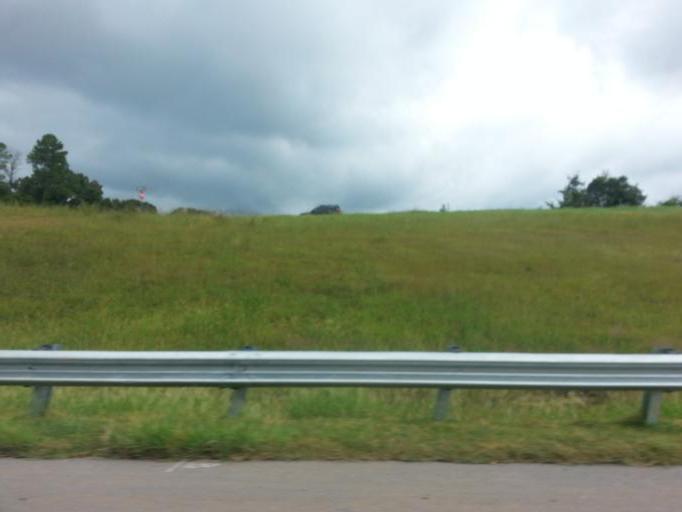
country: US
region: Alabama
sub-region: Conecuh County
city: Evergreen
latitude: 31.3295
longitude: -87.1265
